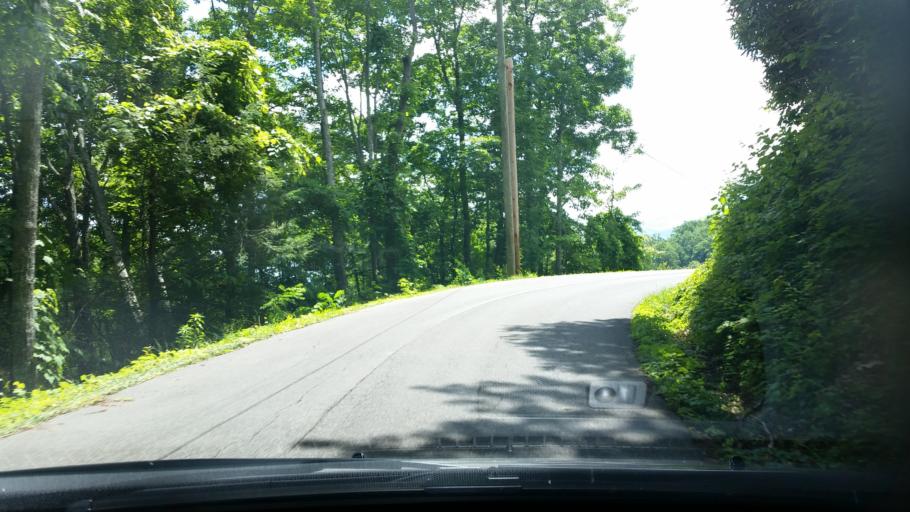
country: US
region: Tennessee
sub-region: Sevier County
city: Gatlinburg
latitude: 35.7099
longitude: -83.5518
